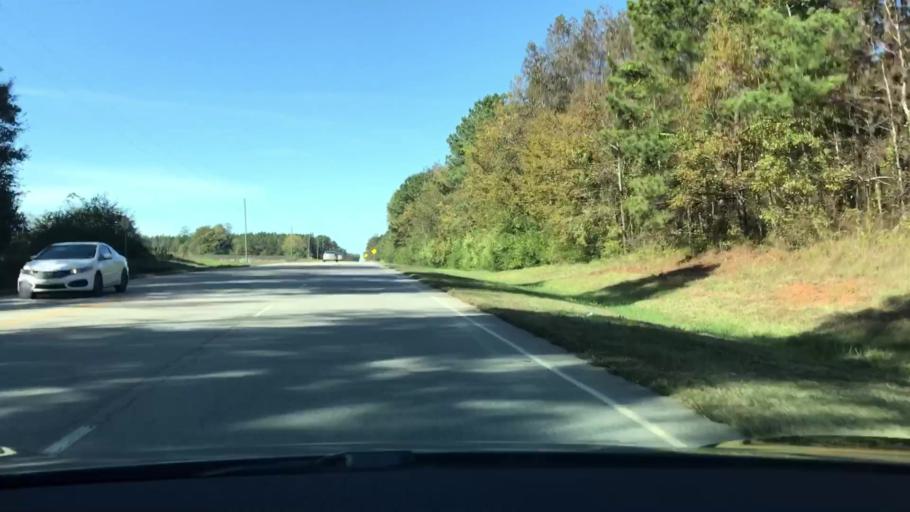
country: US
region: Georgia
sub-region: Warren County
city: Firing Range
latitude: 33.4797
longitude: -82.7479
